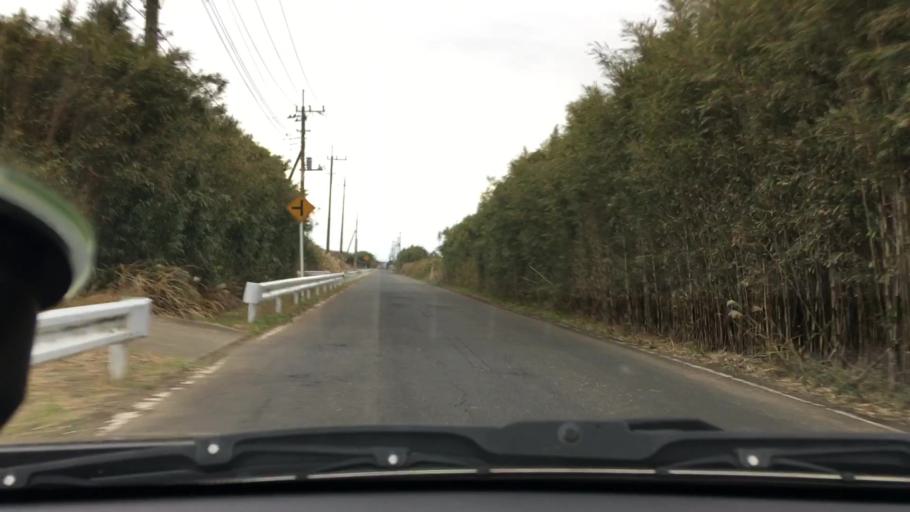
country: JP
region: Chiba
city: Omigawa
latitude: 35.8790
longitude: 140.6752
